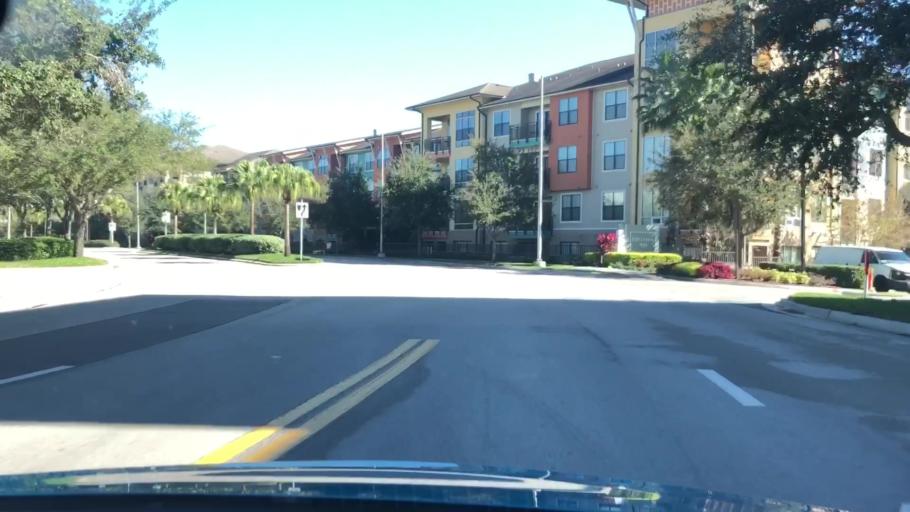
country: US
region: Florida
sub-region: Orange County
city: Oak Ridge
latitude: 28.4826
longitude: -81.4311
